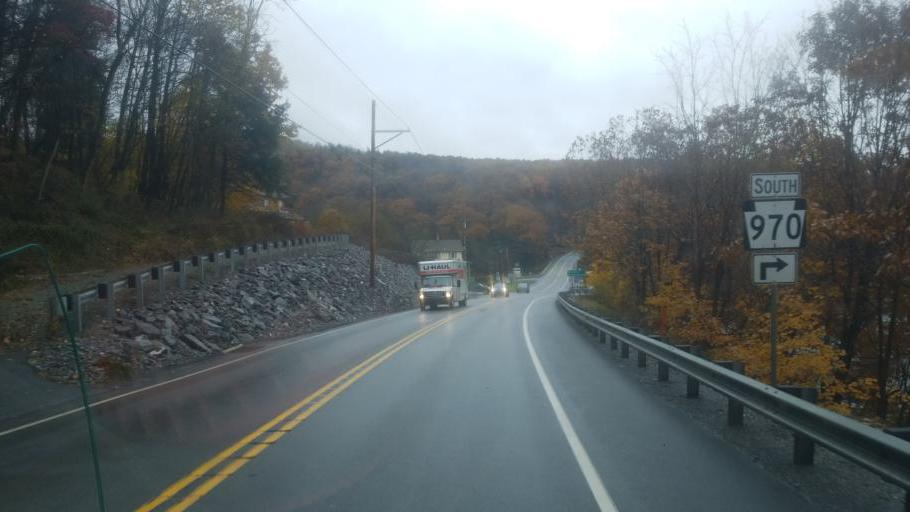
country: US
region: Pennsylvania
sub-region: Clearfield County
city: Shiloh
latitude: 41.0697
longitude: -78.3630
